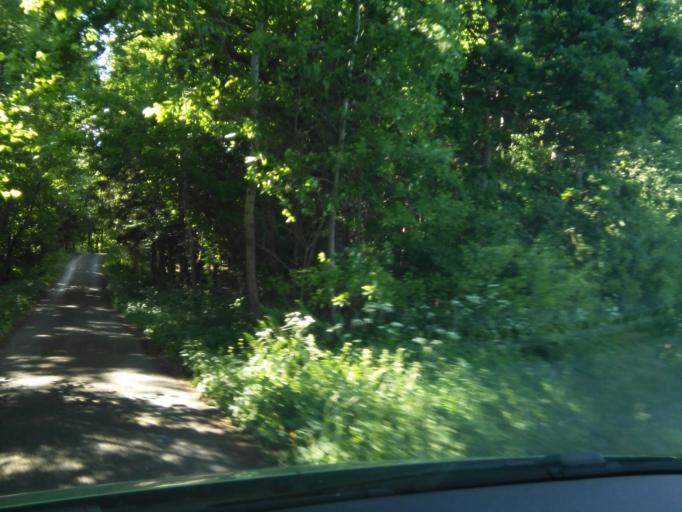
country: DK
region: Capital Region
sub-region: Bornholm Kommune
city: Nexo
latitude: 55.0841
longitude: 15.0742
